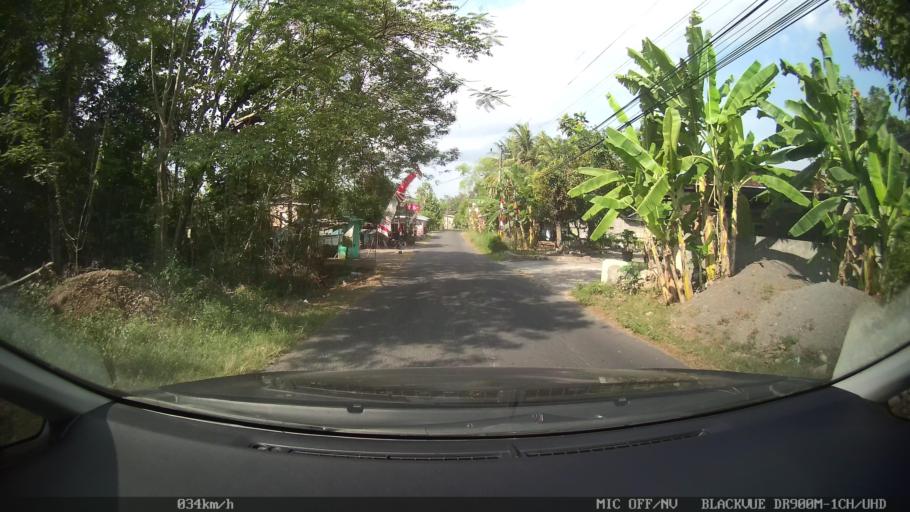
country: ID
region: Daerah Istimewa Yogyakarta
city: Kasihan
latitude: -7.8419
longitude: 110.3064
